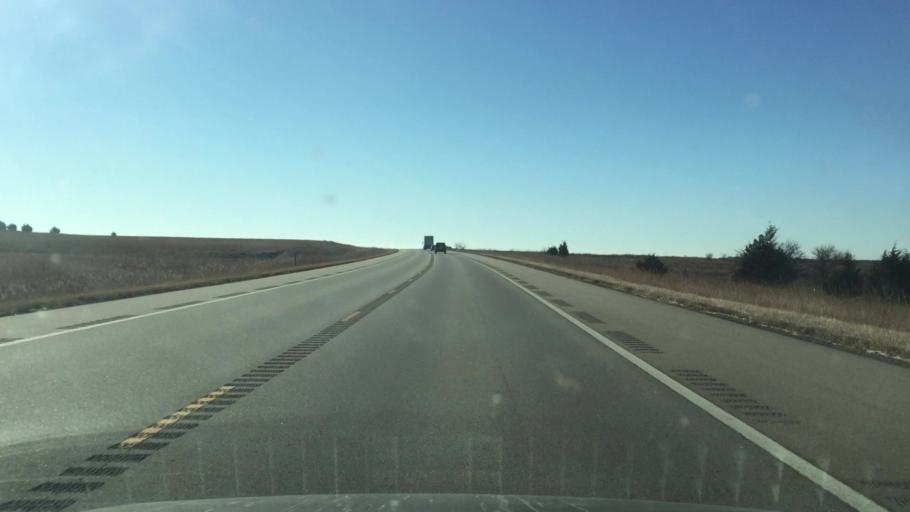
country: US
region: Kansas
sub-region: Allen County
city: Iola
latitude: 38.0638
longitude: -95.3802
